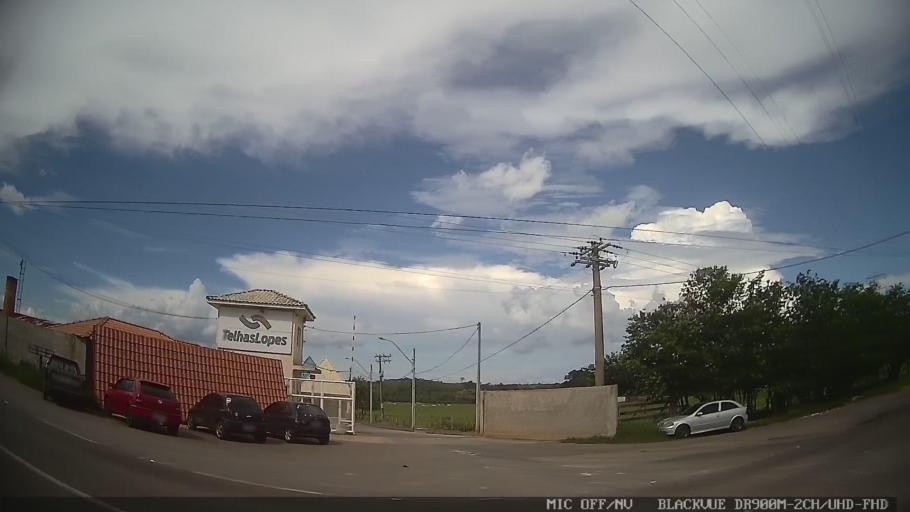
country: BR
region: Sao Paulo
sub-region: Conchas
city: Conchas
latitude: -23.0239
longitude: -47.9965
